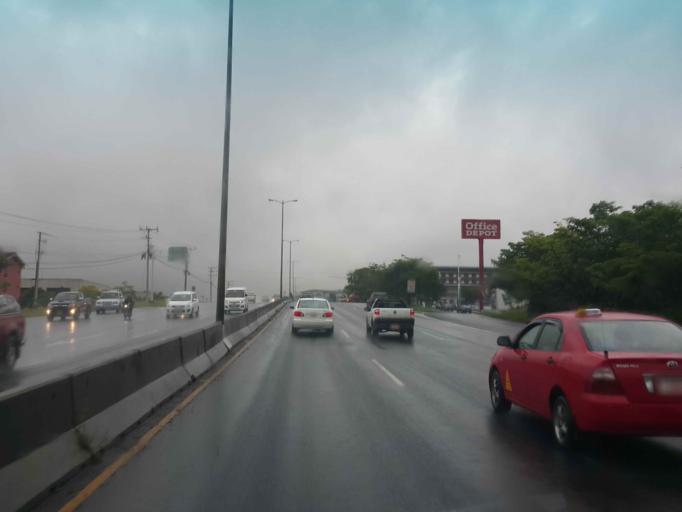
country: CR
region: San Jose
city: San Rafael
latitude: 9.9433
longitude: -84.1475
